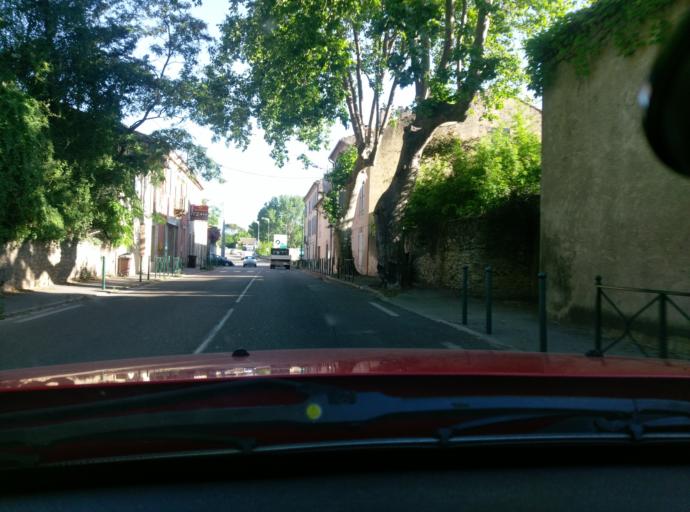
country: FR
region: Languedoc-Roussillon
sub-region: Departement du Gard
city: Remoulins
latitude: 43.9353
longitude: 4.5571
